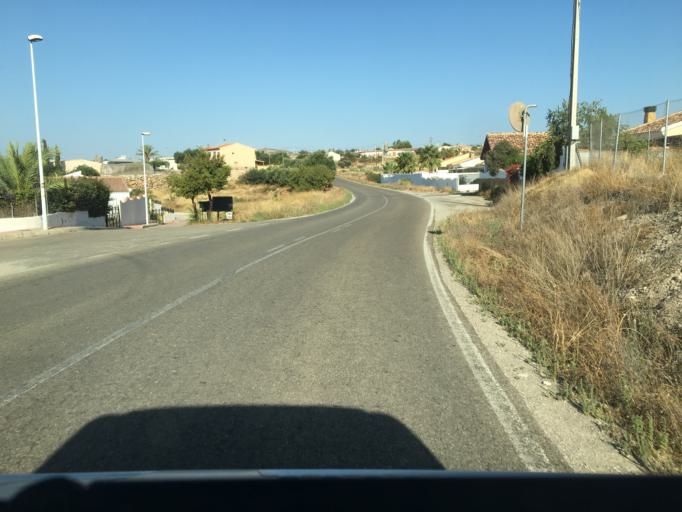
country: ES
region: Andalusia
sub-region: Provincia de Almeria
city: Huercal-Overa
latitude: 37.4694
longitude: -1.9144
